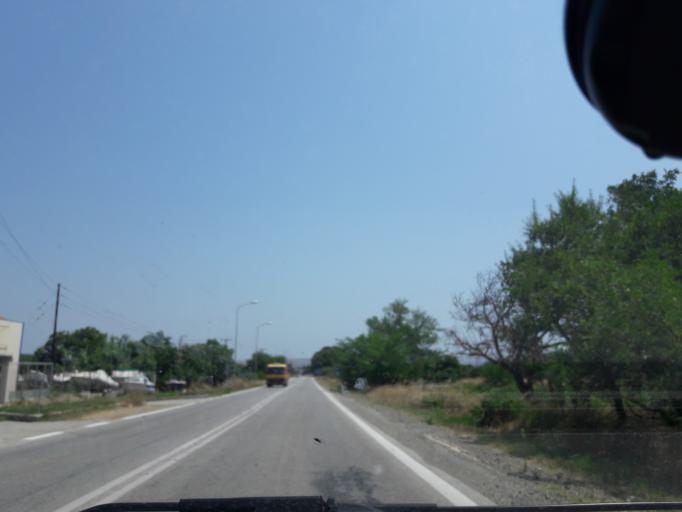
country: GR
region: North Aegean
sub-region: Nomos Lesvou
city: Myrina
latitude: 39.9117
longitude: 25.1915
